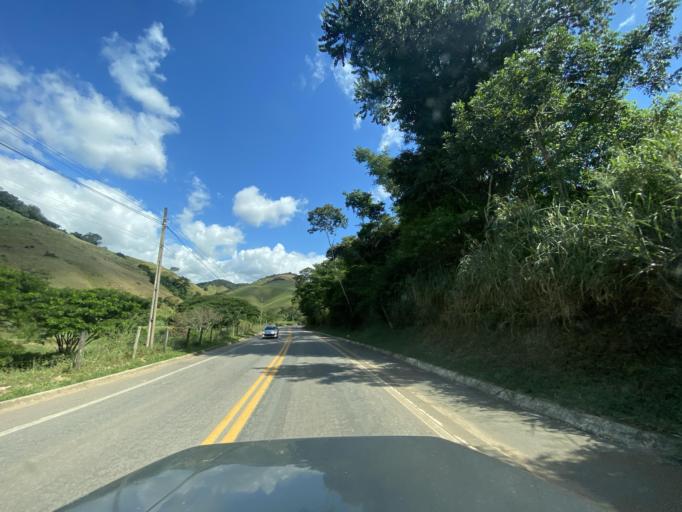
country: BR
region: Espirito Santo
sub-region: Alegre
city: Alegre
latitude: -20.7632
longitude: -41.5059
